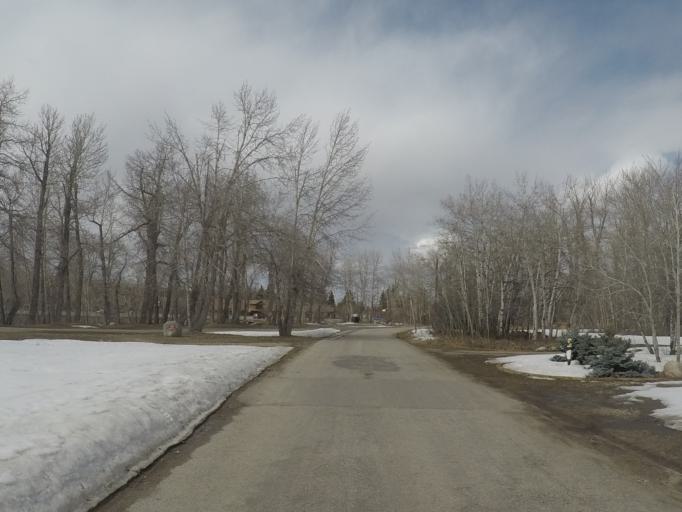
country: US
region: Montana
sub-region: Carbon County
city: Red Lodge
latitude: 45.1757
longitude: -109.2481
